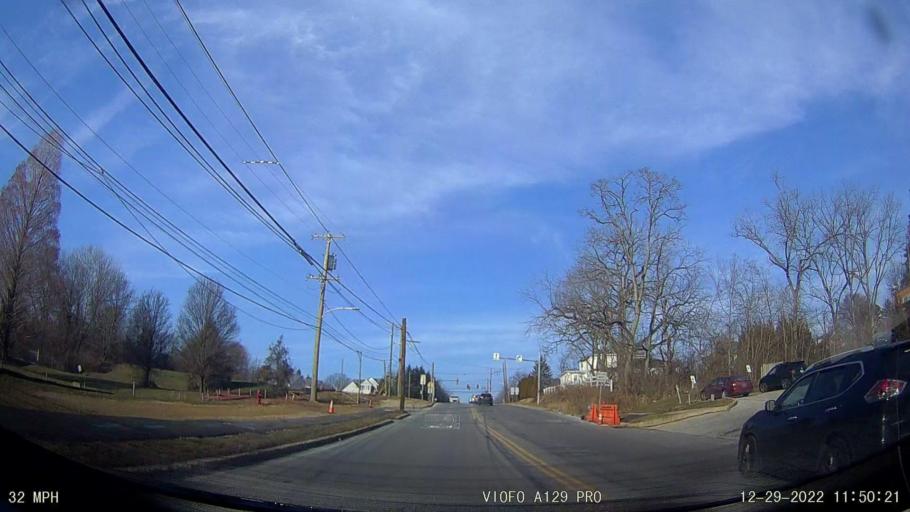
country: US
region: Pennsylvania
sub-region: Montgomery County
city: Norristown
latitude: 40.1283
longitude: -75.3224
